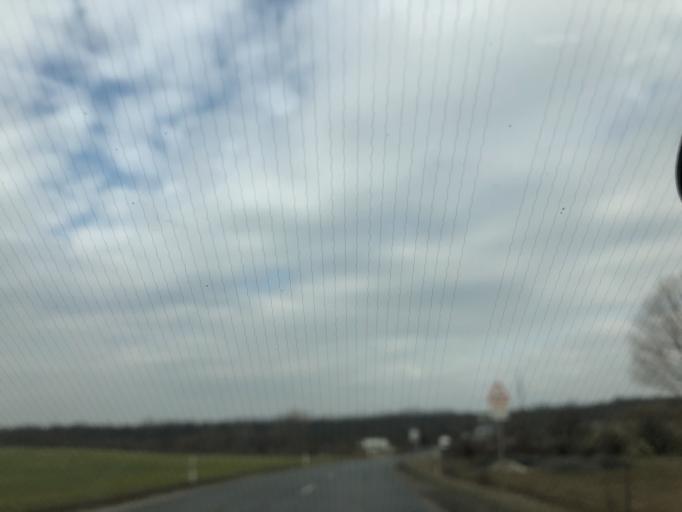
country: HU
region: Fejer
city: Bicske
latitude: 47.4794
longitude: 18.5747
